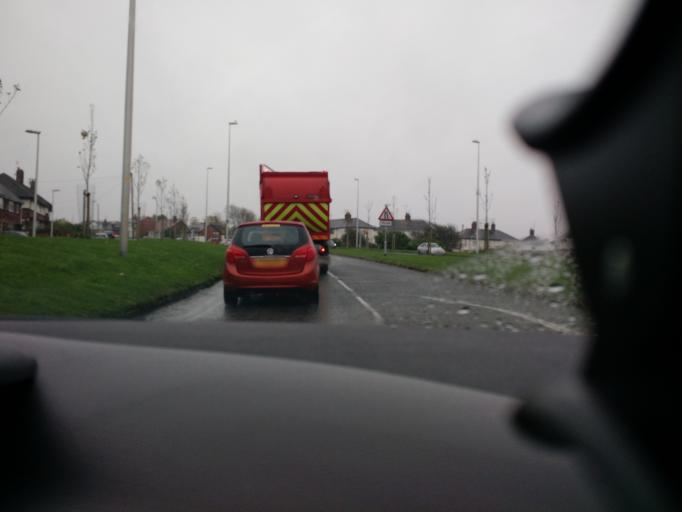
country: GB
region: England
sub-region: Lancashire
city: Great Marton
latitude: 53.8291
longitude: -3.0248
